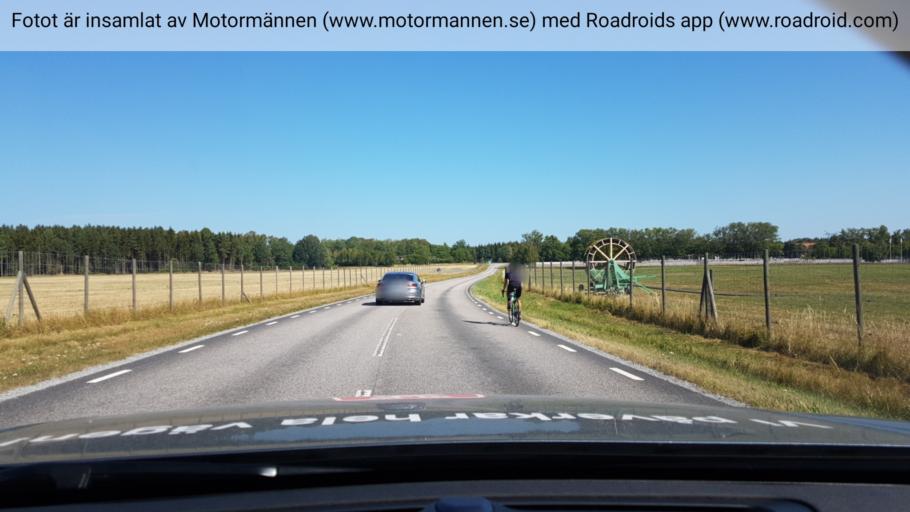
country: SE
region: Stockholm
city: Stenhamra
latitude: 59.3214
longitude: 17.6319
